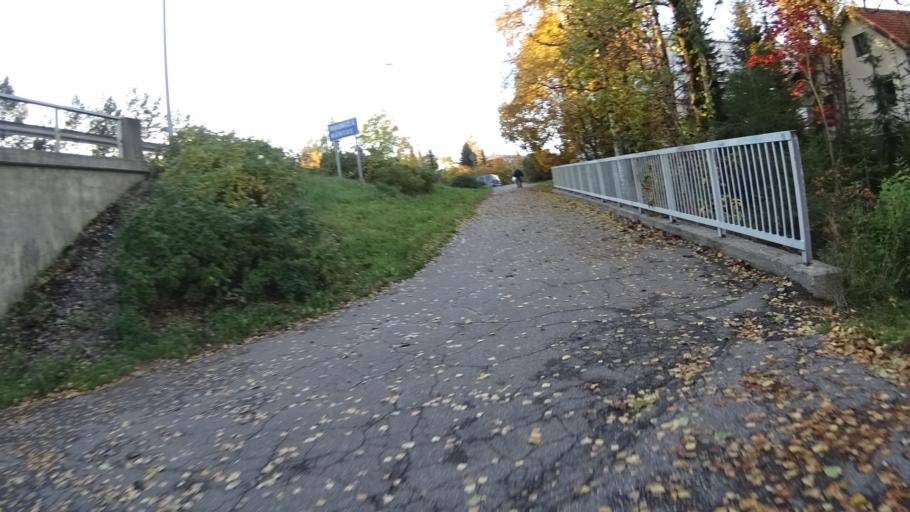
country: FI
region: Uusimaa
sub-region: Helsinki
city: Helsinki
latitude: 60.2296
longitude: 24.9399
